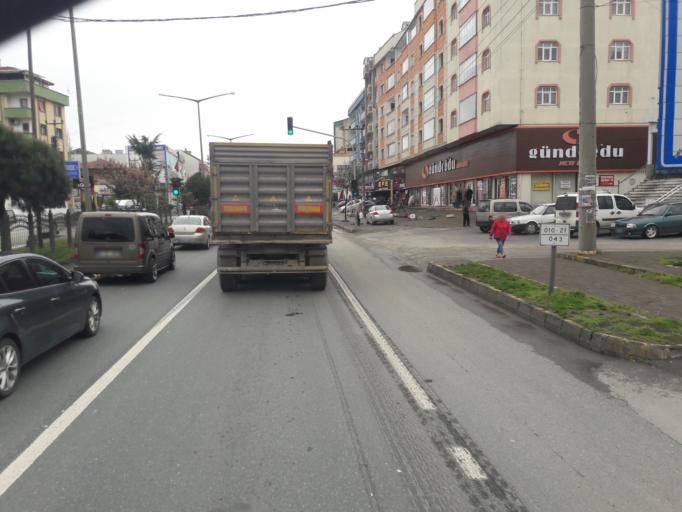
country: TR
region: Trabzon
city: Akcaabat
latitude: 41.0132
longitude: 39.6060
